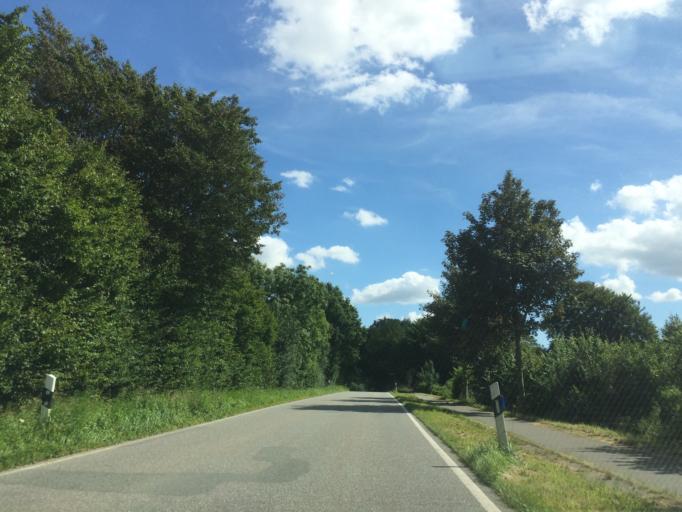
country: DE
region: Schleswig-Holstein
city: Grebin
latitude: 54.1906
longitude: 10.5215
